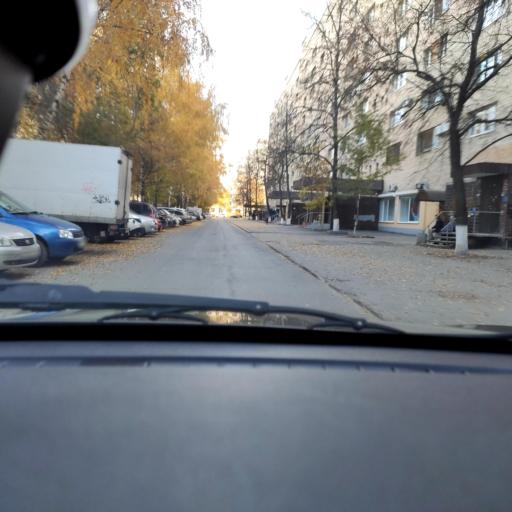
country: RU
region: Samara
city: Tol'yatti
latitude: 53.5277
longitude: 49.2716
